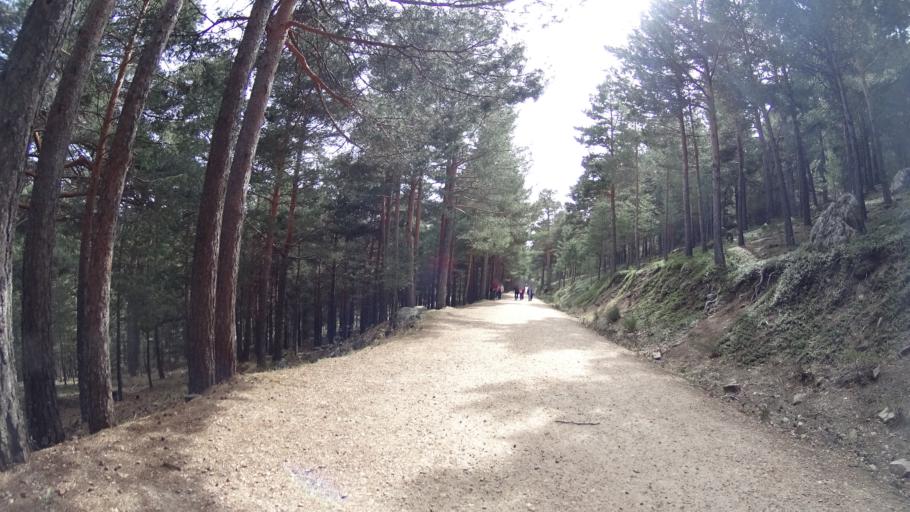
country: ES
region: Madrid
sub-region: Provincia de Madrid
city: Navacerrada
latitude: 40.7634
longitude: -3.9961
